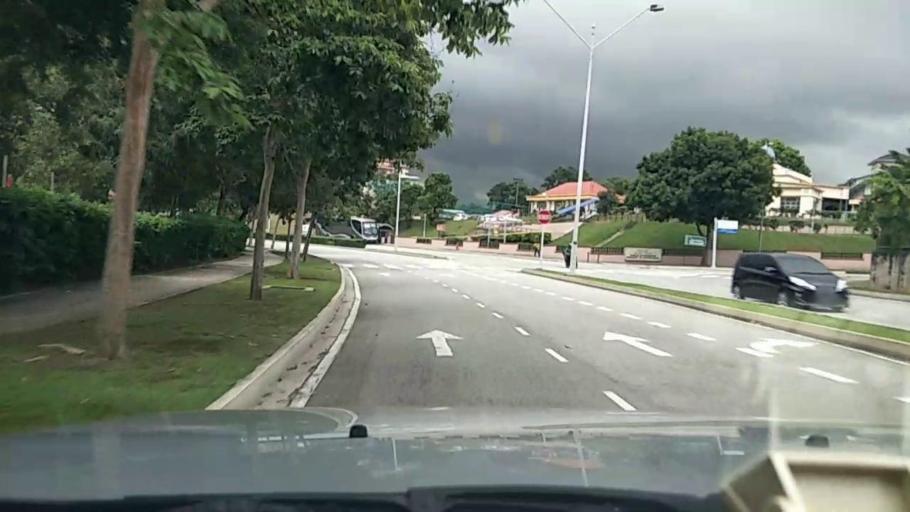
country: MY
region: Putrajaya
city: Putrajaya
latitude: 2.9322
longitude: 101.7061
